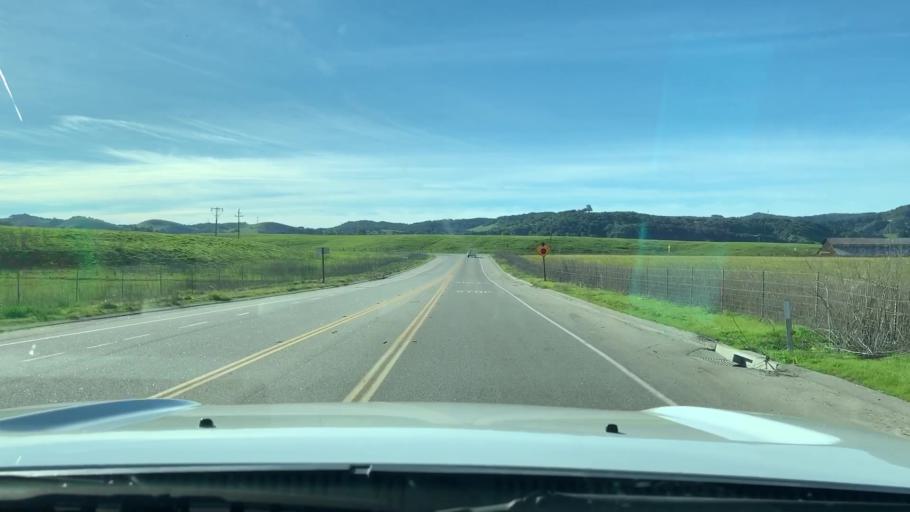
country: US
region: California
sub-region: San Luis Obispo County
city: San Luis Obispo
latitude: 35.2379
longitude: -120.6509
